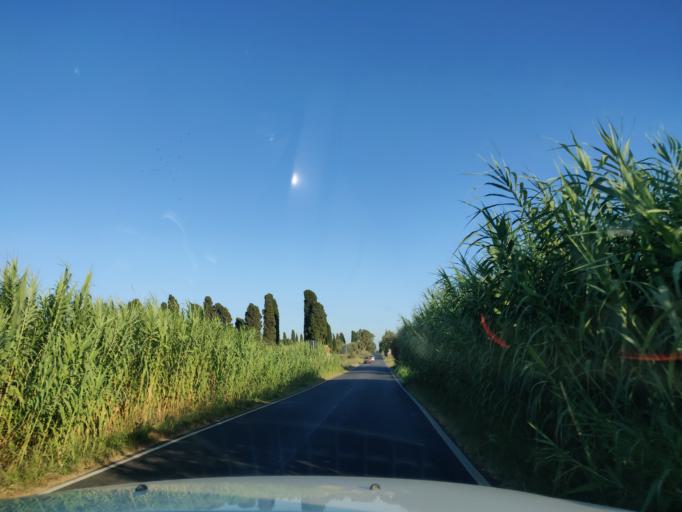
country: IT
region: Latium
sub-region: Provincia di Viterbo
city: Montalto di Castro
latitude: 42.2878
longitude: 11.6625
